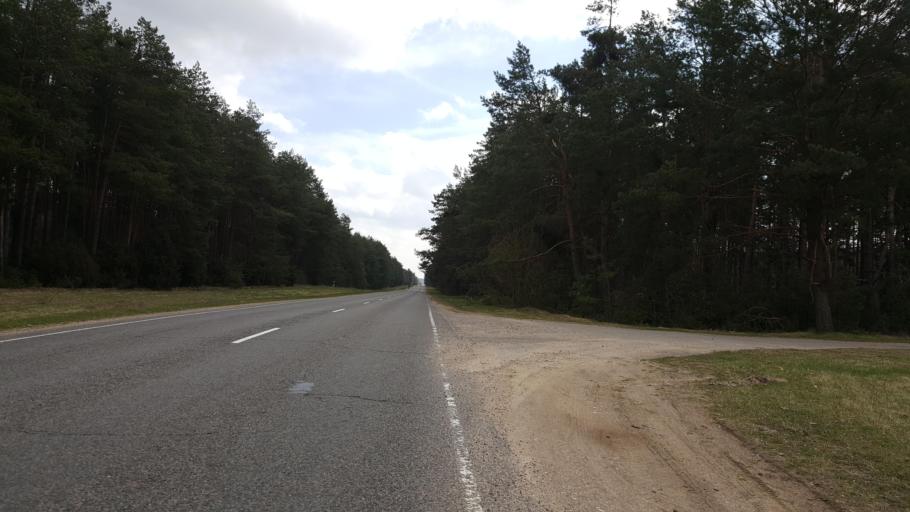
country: BY
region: Brest
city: Kamyanyets
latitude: 52.3834
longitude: 23.8600
